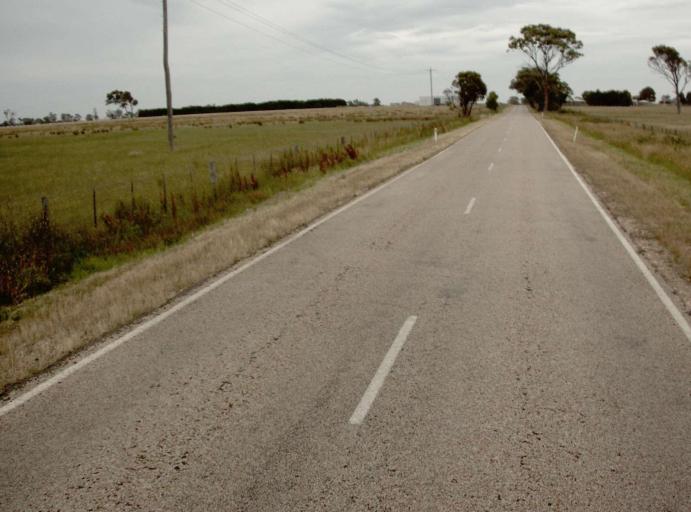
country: AU
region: Victoria
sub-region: East Gippsland
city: Bairnsdale
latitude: -37.8514
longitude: 147.4290
